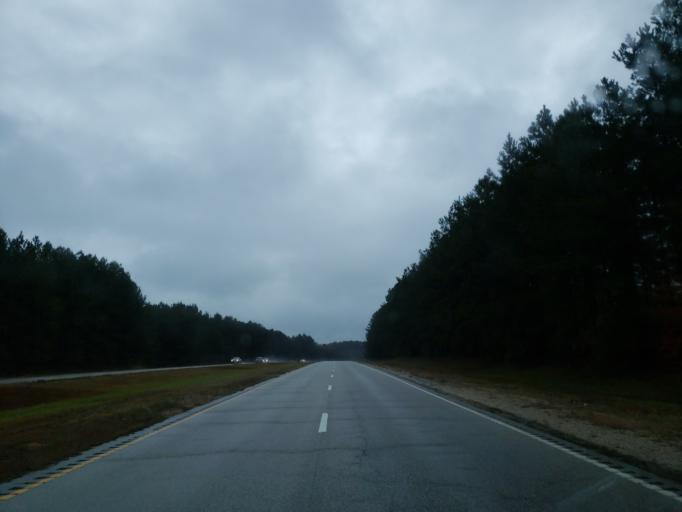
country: US
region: Mississippi
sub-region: Lauderdale County
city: Meridian
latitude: 32.2946
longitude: -88.6956
